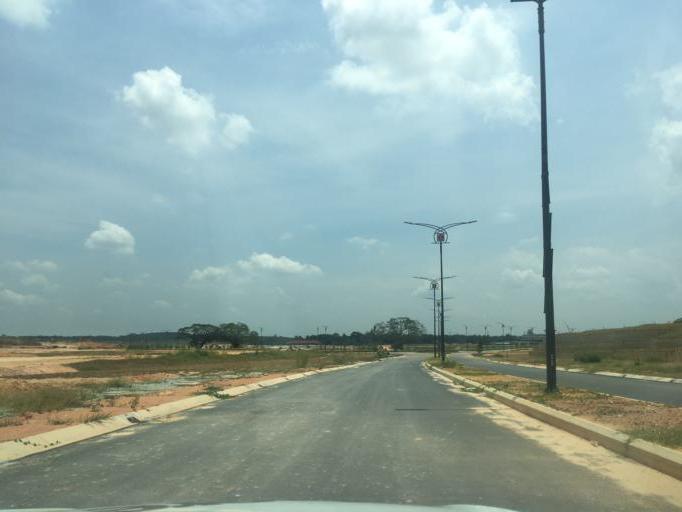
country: MY
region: Putrajaya
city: Putrajaya
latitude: 2.8450
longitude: 101.7087
